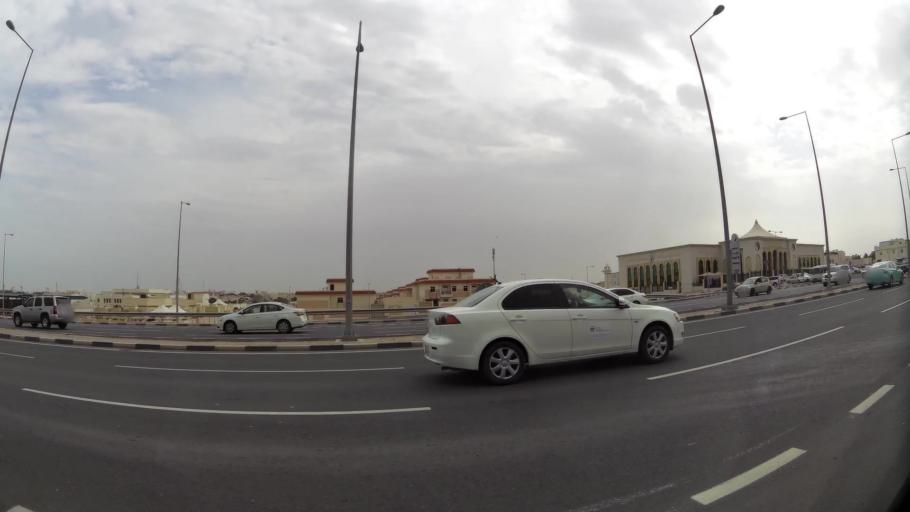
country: QA
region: Baladiyat ad Dawhah
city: Doha
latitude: 25.3353
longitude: 51.4908
